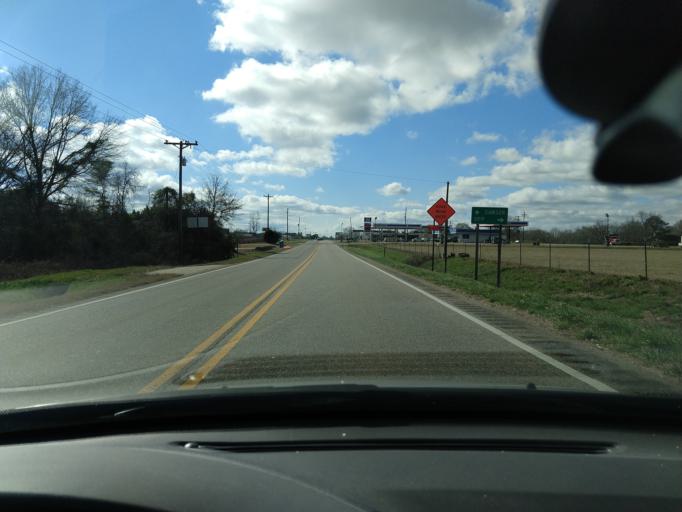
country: US
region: Alabama
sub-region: Coffee County
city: Elba
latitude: 31.3057
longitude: -86.0372
